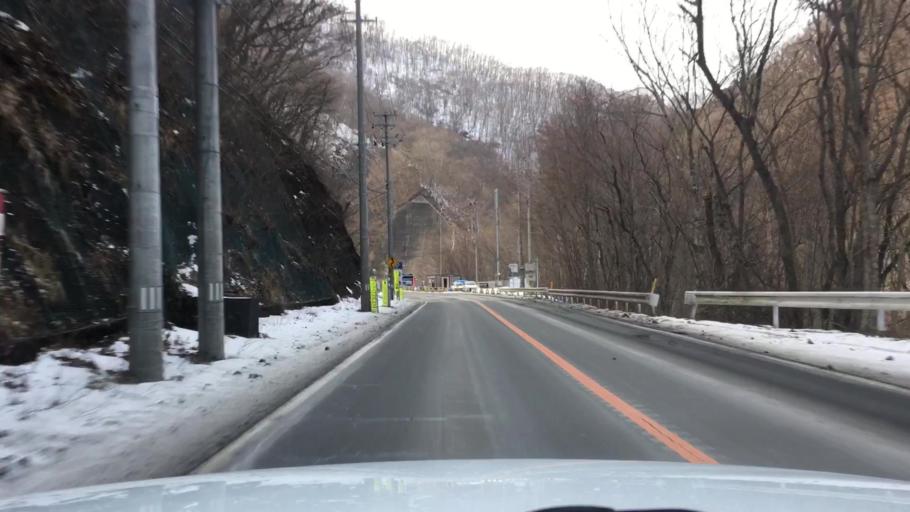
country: JP
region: Iwate
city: Tono
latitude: 39.6314
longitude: 141.5262
